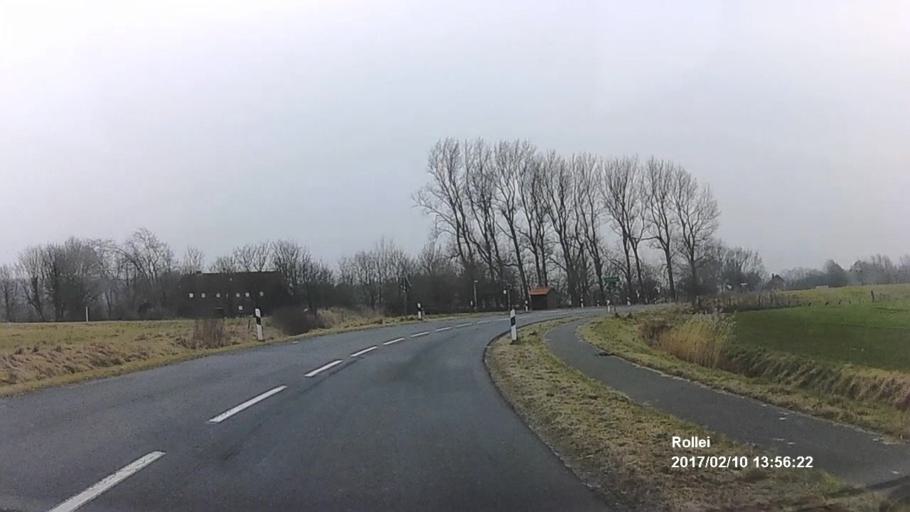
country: DE
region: Lower Saxony
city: Norddeich
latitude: 53.5497
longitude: 7.1523
